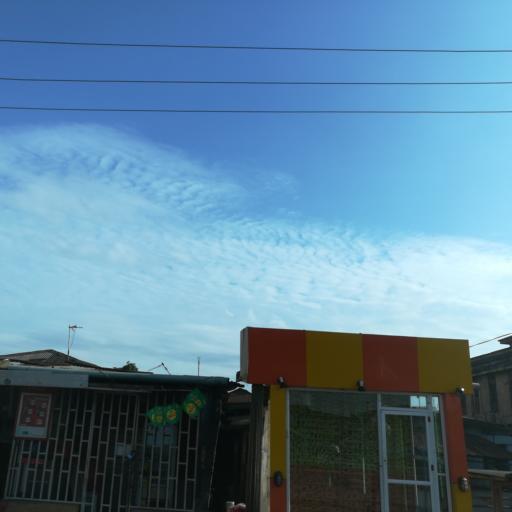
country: NG
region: Lagos
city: Agege
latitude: 6.6151
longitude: 3.3251
